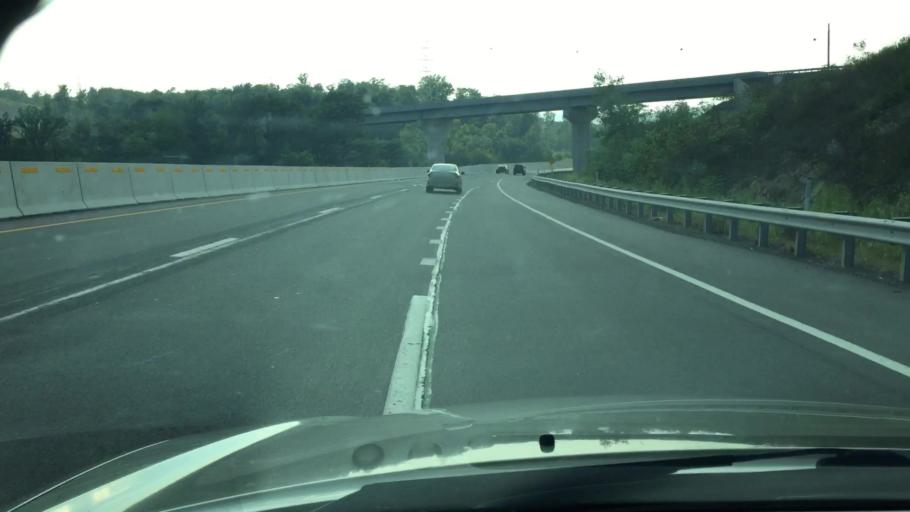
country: US
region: Pennsylvania
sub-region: Luzerne County
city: Nanticoke
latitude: 41.1996
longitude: -75.9623
